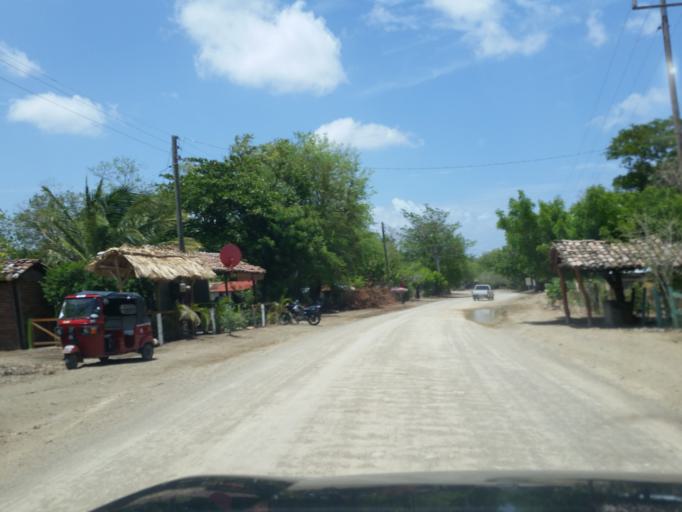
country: NI
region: Rivas
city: Tola
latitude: 11.4614
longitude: -86.0807
